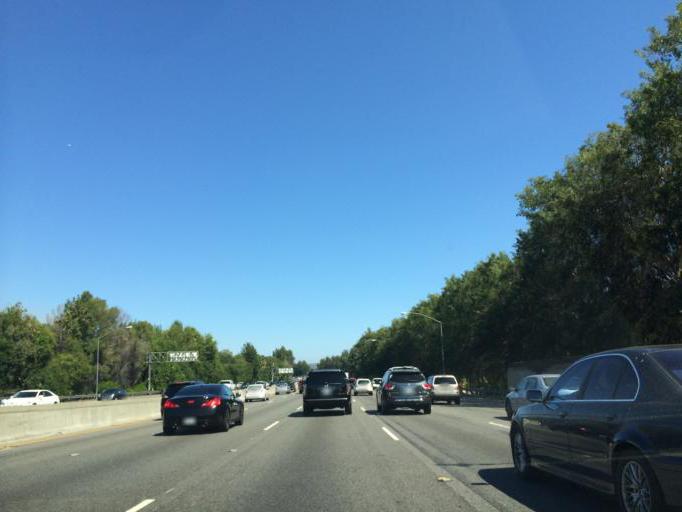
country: US
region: California
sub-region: Los Angeles County
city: Sherman Oaks
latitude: 34.1688
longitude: -118.4985
